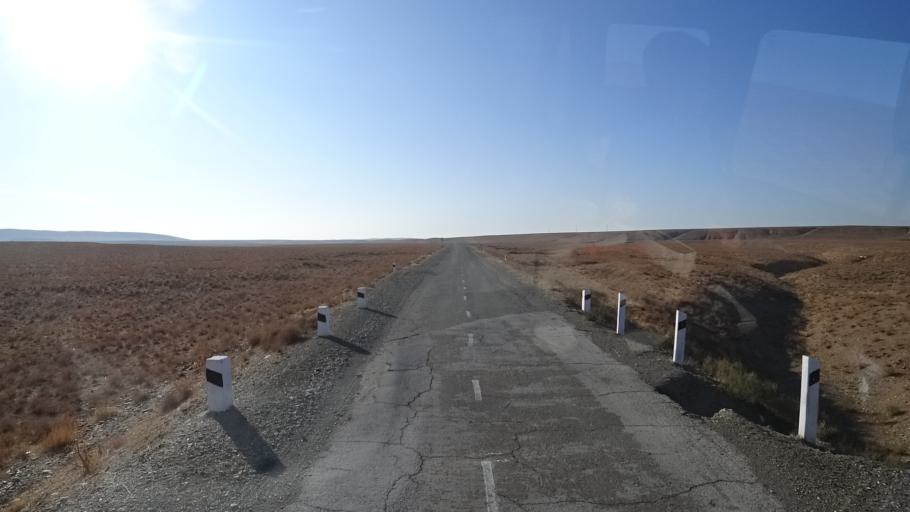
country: UZ
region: Navoiy
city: Beshrabot
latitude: 40.2609
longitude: 65.4939
